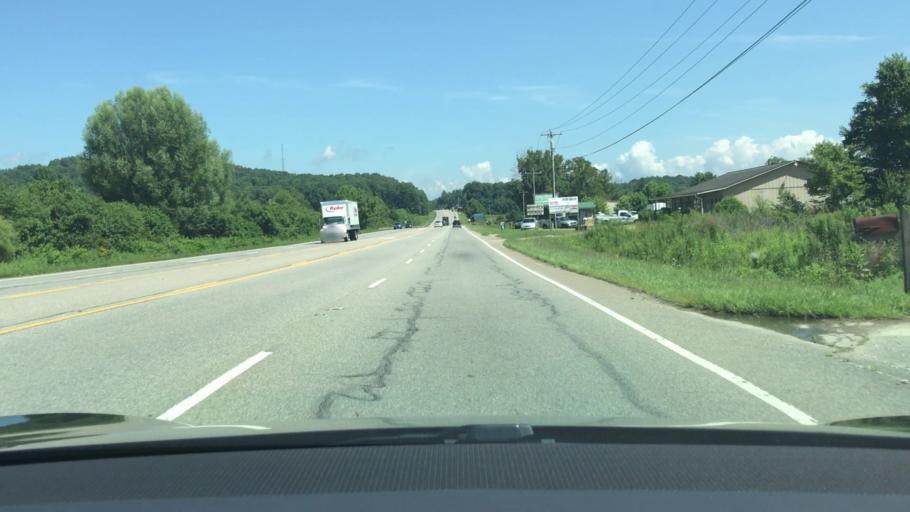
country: US
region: North Carolina
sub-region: Macon County
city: Franklin
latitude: 35.0952
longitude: -83.3839
